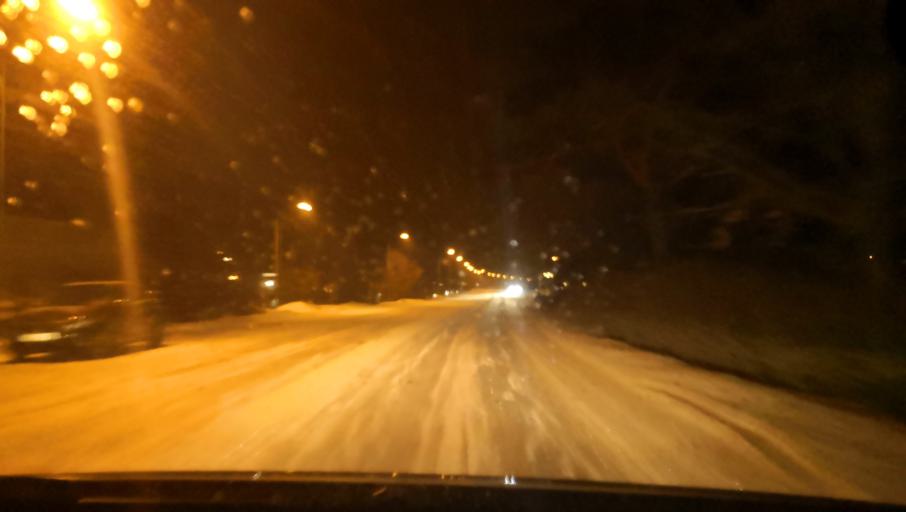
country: SE
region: Uppsala
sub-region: Heby Kommun
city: Tarnsjo
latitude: 60.1614
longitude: 16.9378
